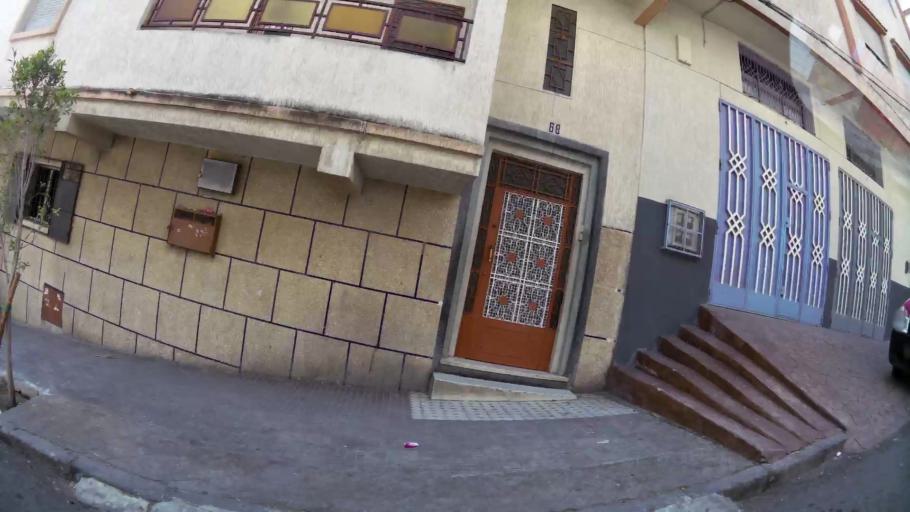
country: MA
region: Tanger-Tetouan
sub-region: Tanger-Assilah
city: Tangier
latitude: 35.7740
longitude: -5.8255
